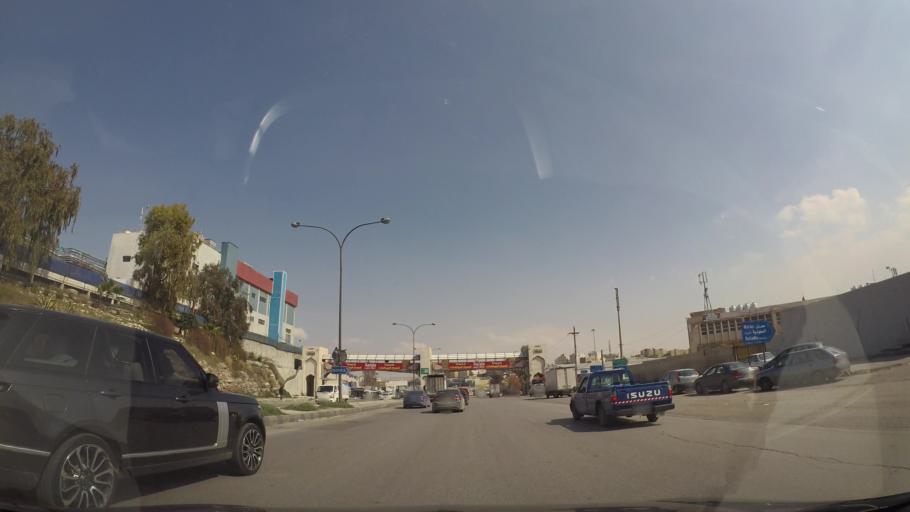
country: JO
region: Zarqa
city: Russeifa
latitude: 31.9959
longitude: 36.0189
